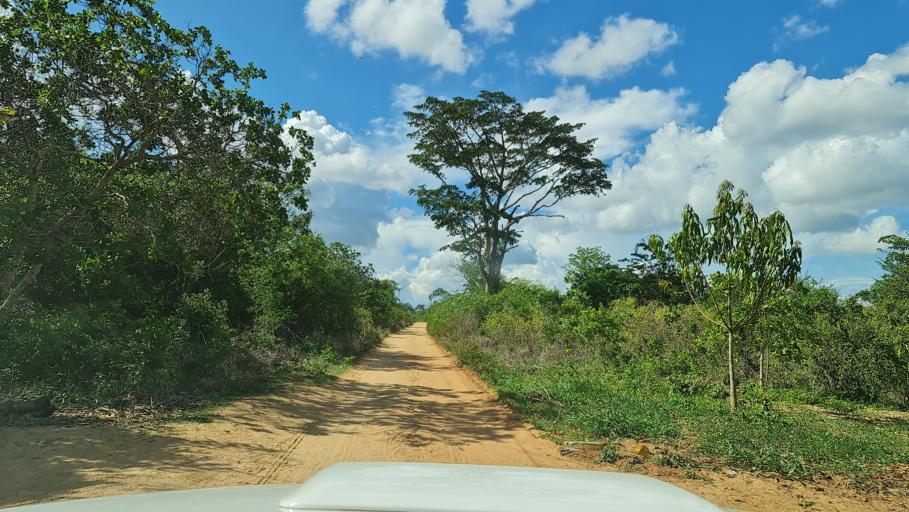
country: MZ
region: Nampula
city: Ilha de Mocambique
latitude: -15.4331
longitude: 40.2754
